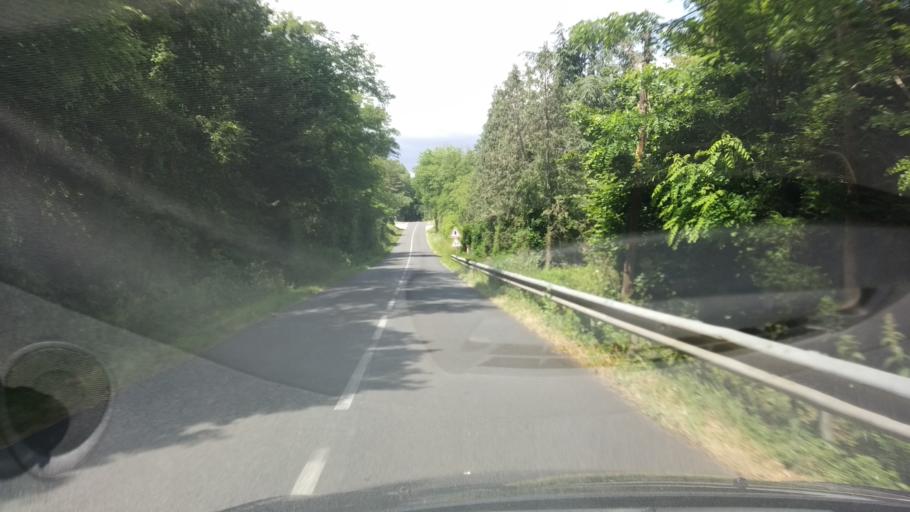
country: FR
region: Poitou-Charentes
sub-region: Departement de la Vienne
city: Cisse
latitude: 46.6145
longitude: 0.2213
